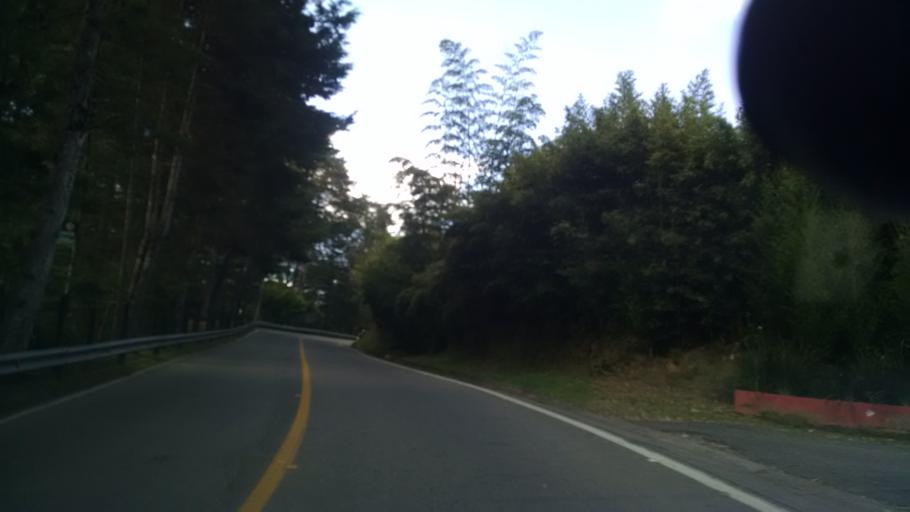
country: CO
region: Antioquia
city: El Retiro
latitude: 6.0824
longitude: -75.4936
